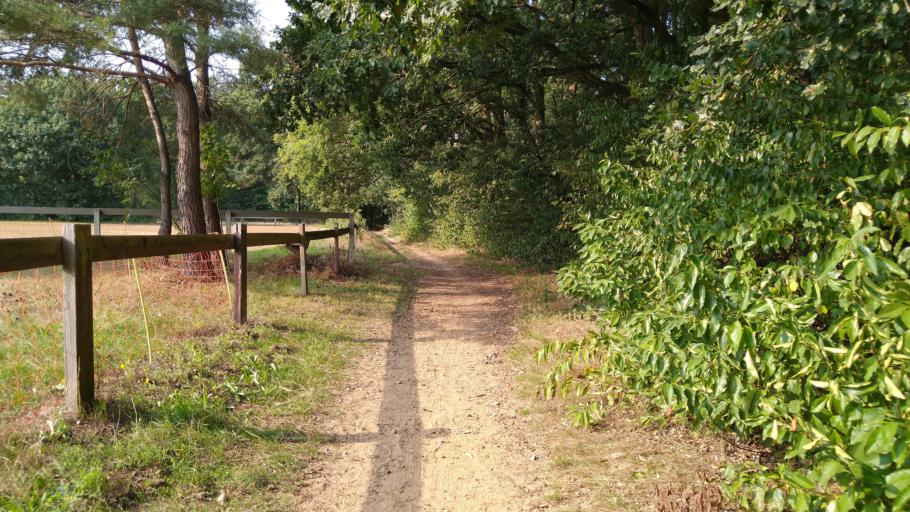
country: BE
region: Flanders
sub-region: Provincie Limburg
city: Heusden
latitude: 51.0235
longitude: 5.2515
